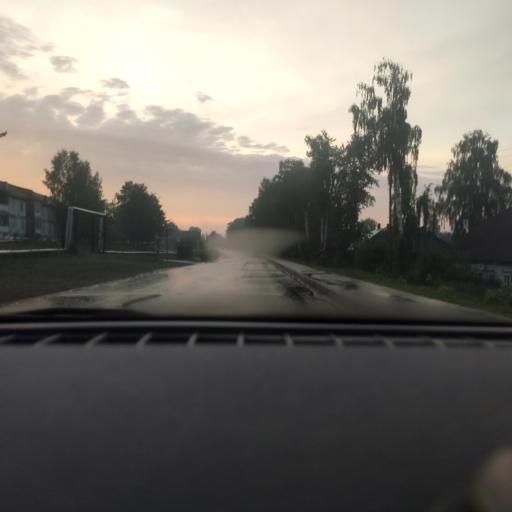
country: RU
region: Perm
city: Nytva
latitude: 57.8981
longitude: 55.4839
